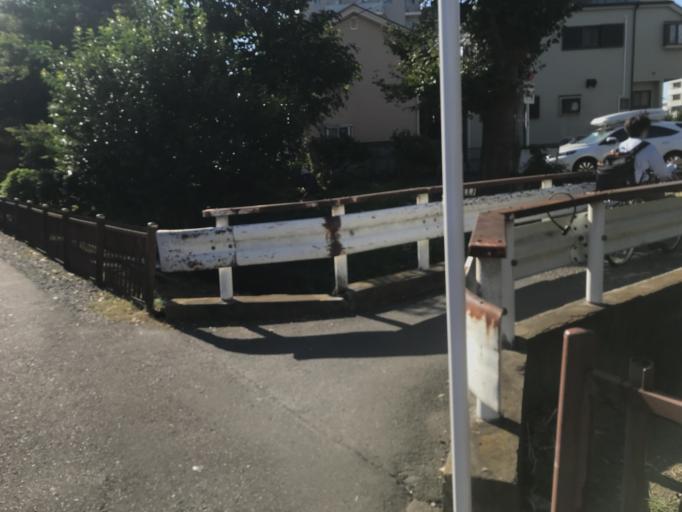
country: JP
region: Tokyo
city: Higashimurayama-shi
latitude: 35.7425
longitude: 139.4634
